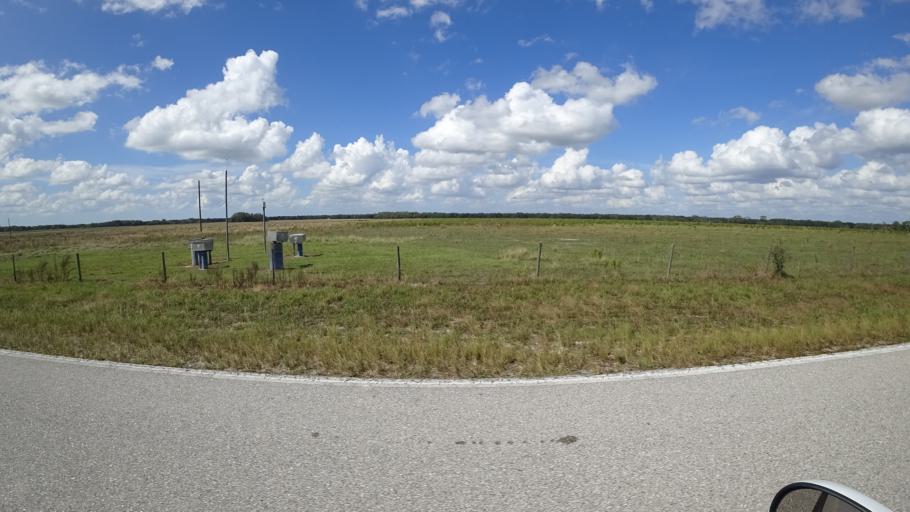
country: US
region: Florida
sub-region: Sarasota County
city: Lake Sarasota
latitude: 27.3148
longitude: -82.1774
